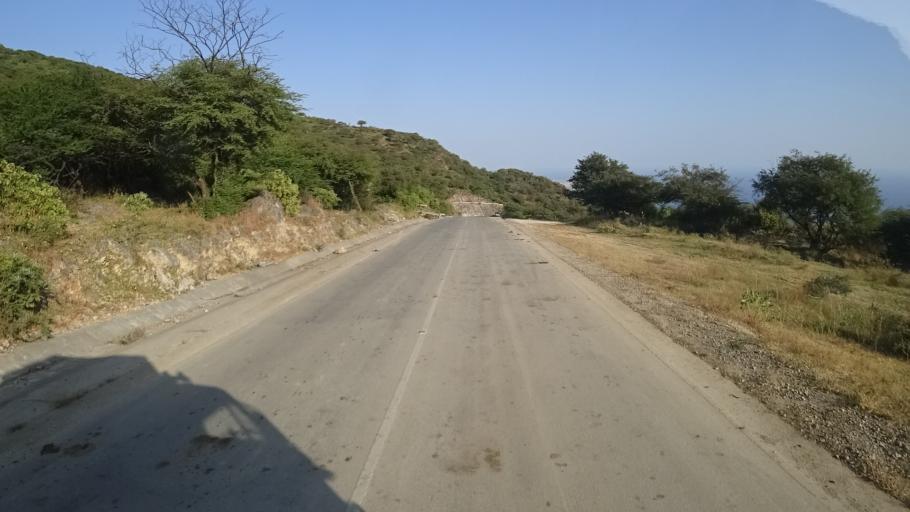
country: OM
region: Zufar
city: Salalah
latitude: 17.0606
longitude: 54.6101
